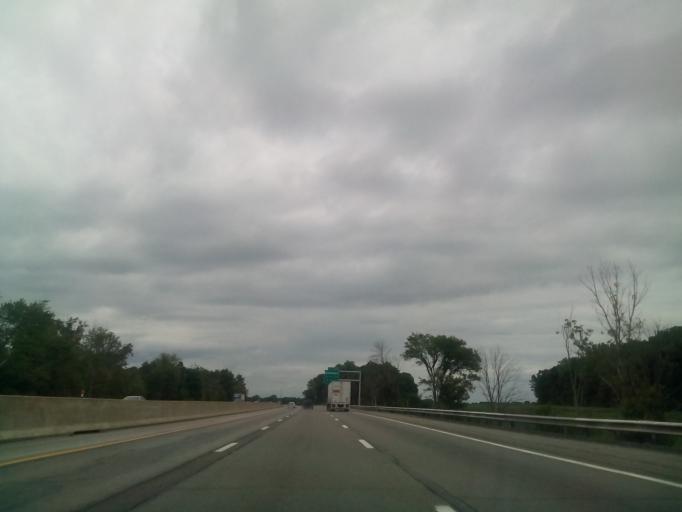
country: US
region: Ohio
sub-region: Lorain County
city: South Amherst
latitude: 41.3456
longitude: -82.3271
